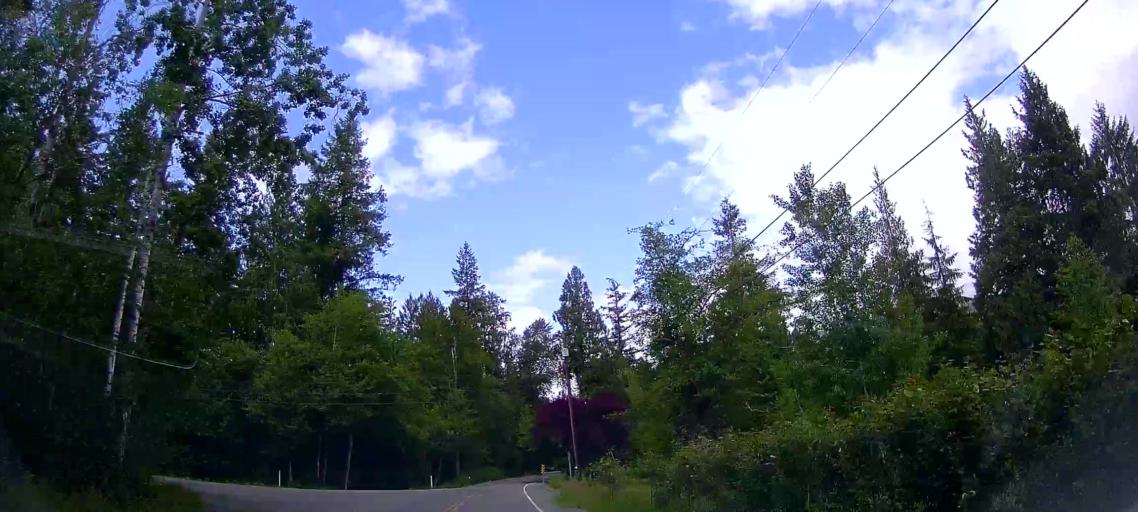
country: US
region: Washington
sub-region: Skagit County
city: Sedro-Woolley
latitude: 48.5375
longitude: -122.2224
